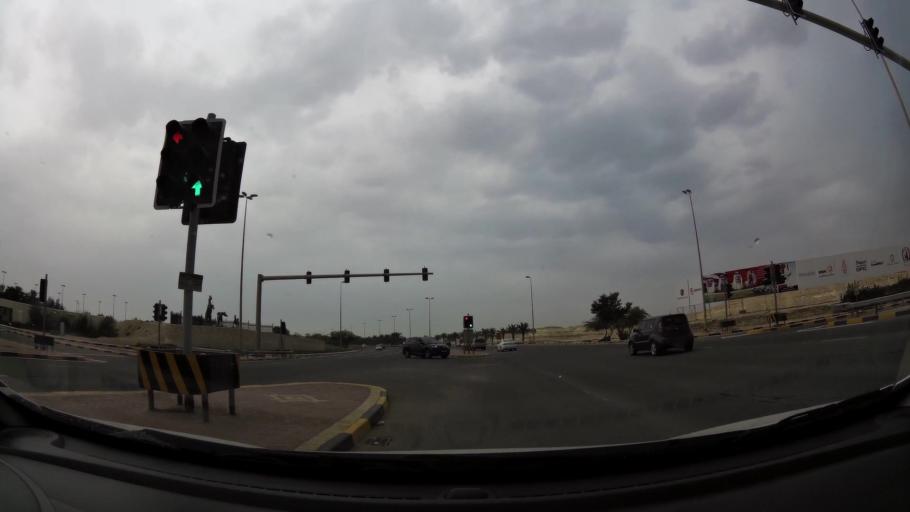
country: BH
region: Central Governorate
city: Dar Kulayb
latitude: 26.0711
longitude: 50.5247
